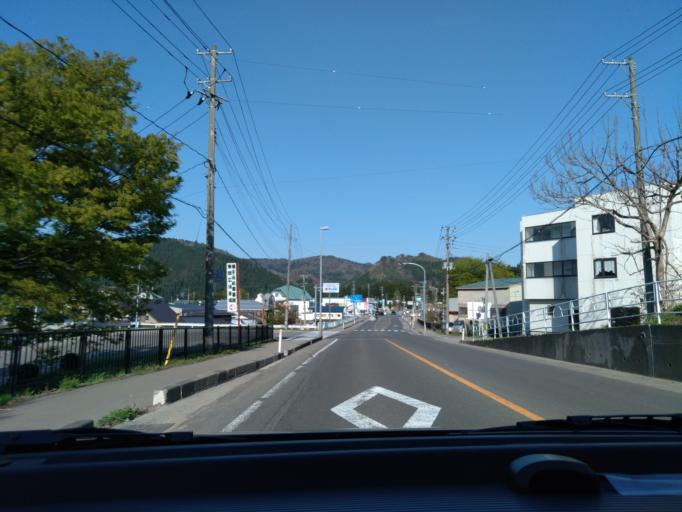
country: JP
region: Akita
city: Yokotemachi
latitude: 39.3053
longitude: 140.5728
